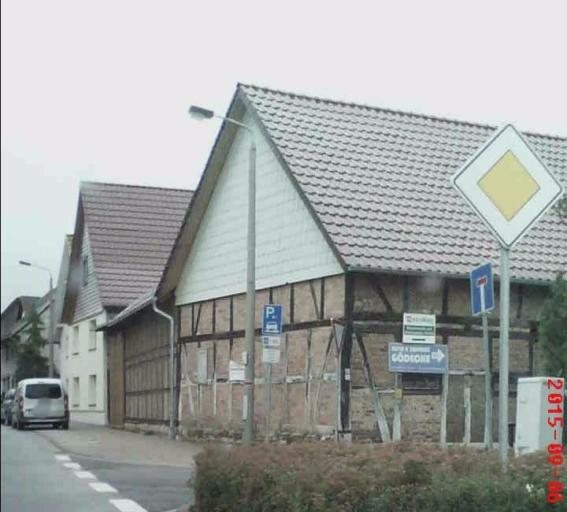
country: DE
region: Thuringia
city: Weissenborn-Luderode
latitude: 51.5316
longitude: 10.4210
